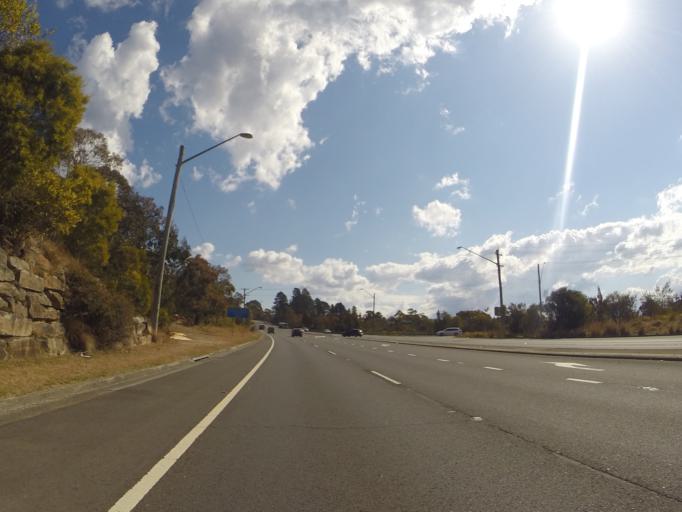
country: AU
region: New South Wales
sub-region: Blue Mountains Municipality
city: Leura
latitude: -33.7094
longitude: 150.3519
